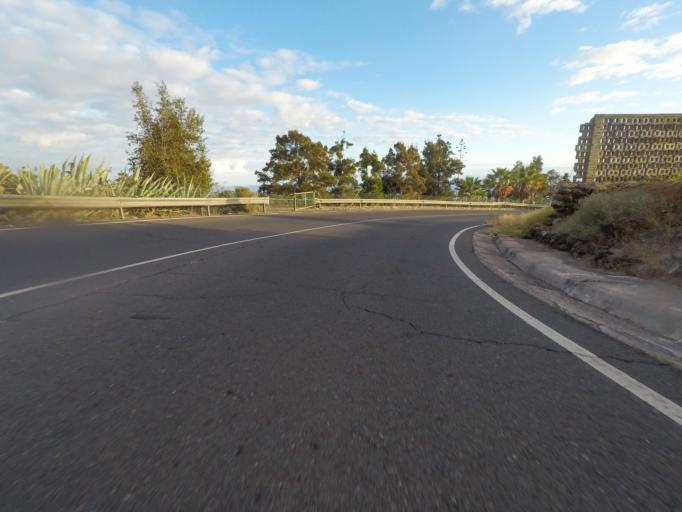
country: ES
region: Canary Islands
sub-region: Provincia de Santa Cruz de Tenerife
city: Alajero
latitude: 28.0372
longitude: -17.1900
